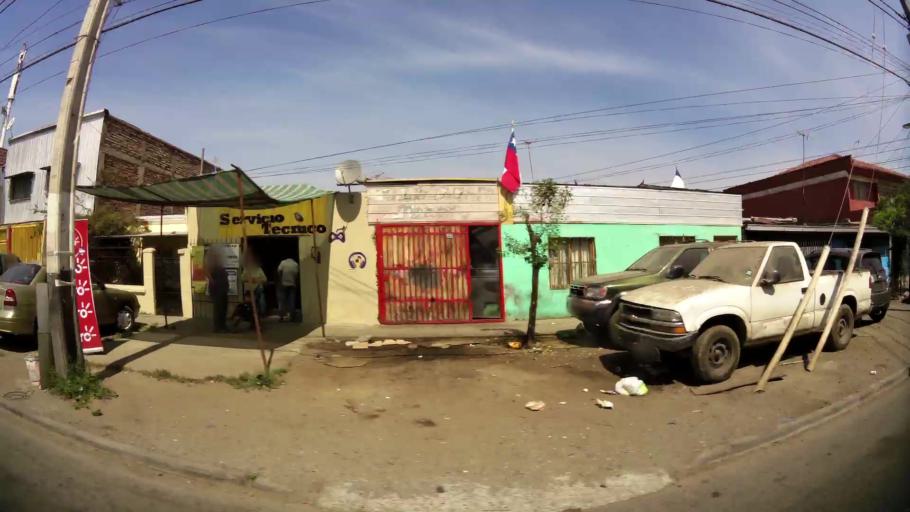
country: CL
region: Santiago Metropolitan
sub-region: Provincia de Santiago
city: Lo Prado
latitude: -33.4197
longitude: -70.7305
